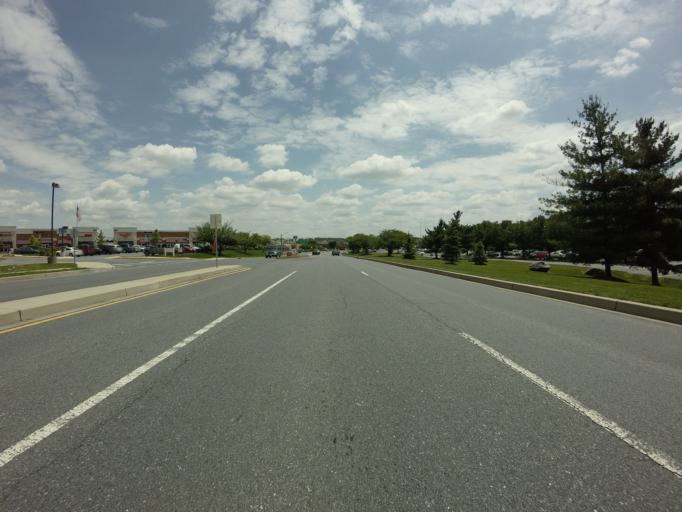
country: US
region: Maryland
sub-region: Frederick County
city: Frederick
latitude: 39.3851
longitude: -77.4062
